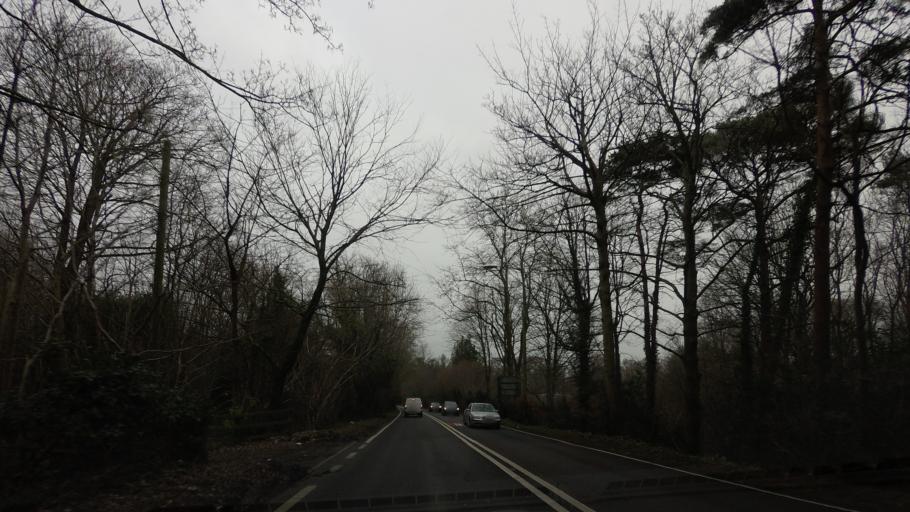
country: GB
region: England
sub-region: East Sussex
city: Saint Leonards-on-Sea
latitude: 50.8938
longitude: 0.5563
